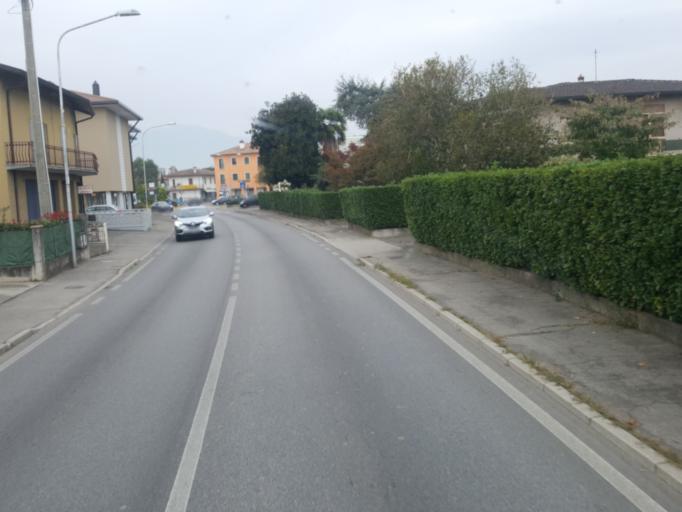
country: IT
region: Veneto
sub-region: Provincia di Treviso
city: Loria Bessica
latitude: 45.7260
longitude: 11.8660
